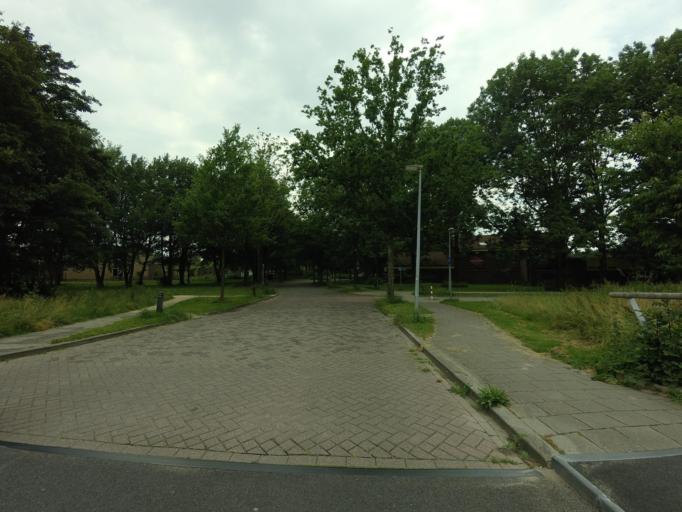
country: NL
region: North Holland
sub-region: Gemeente Hoorn
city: Hoorn
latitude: 52.6499
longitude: 5.0452
